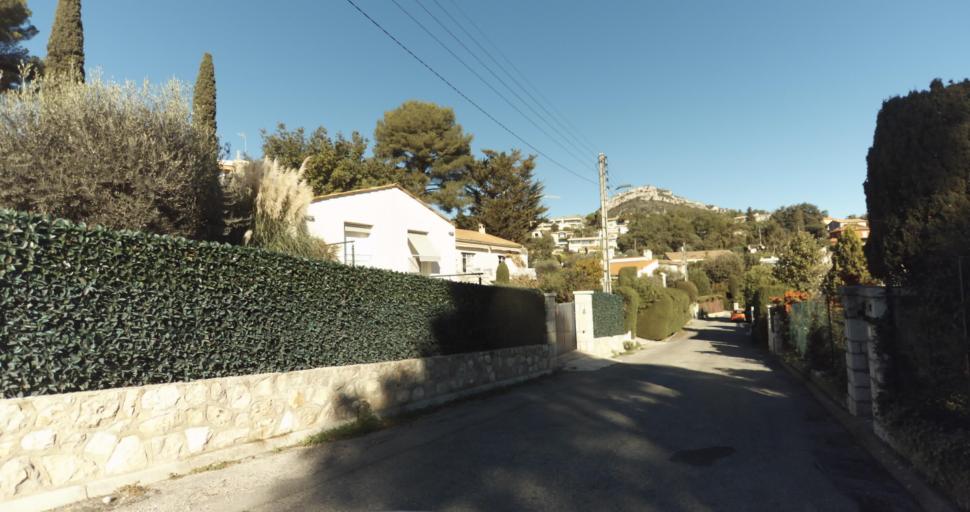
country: FR
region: Provence-Alpes-Cote d'Azur
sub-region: Departement des Alpes-Maritimes
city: Vence
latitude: 43.7189
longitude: 7.1030
